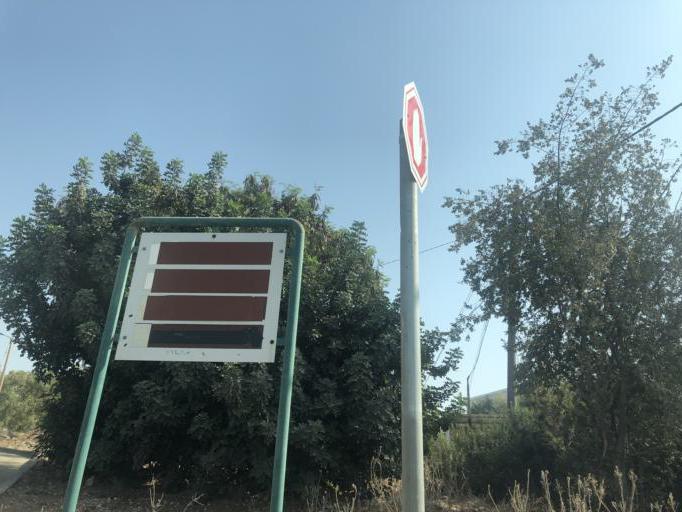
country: IL
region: Central District
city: Rosh Ha'Ayin
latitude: 32.0593
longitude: 34.9492
